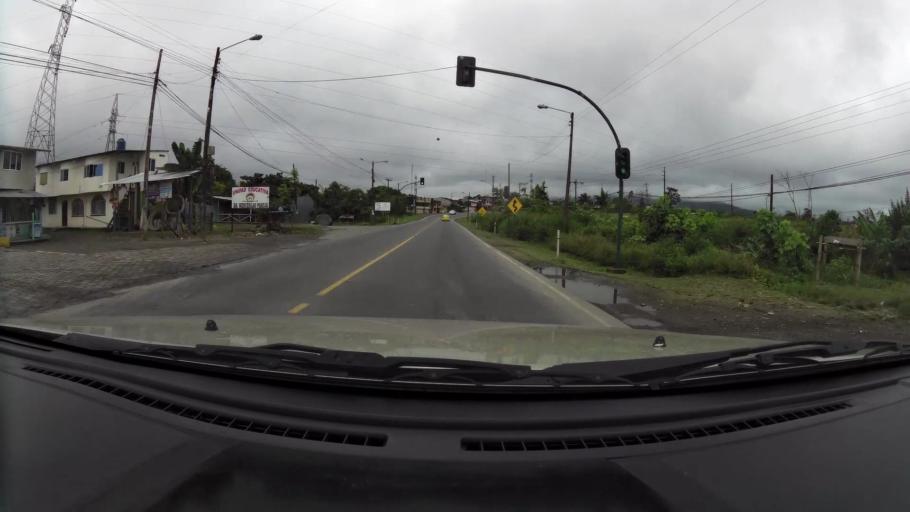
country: EC
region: Santo Domingo de los Tsachilas
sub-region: Canton Santo Domingo de los Colorados
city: Santo Domingo de los Colorados
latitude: -0.2564
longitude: -79.1267
